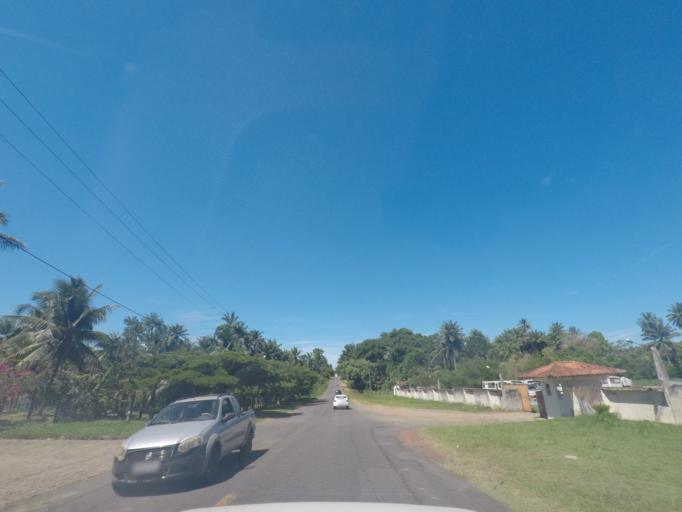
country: BR
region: Bahia
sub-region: Taperoa
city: Taperoa
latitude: -13.4560
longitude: -39.0879
